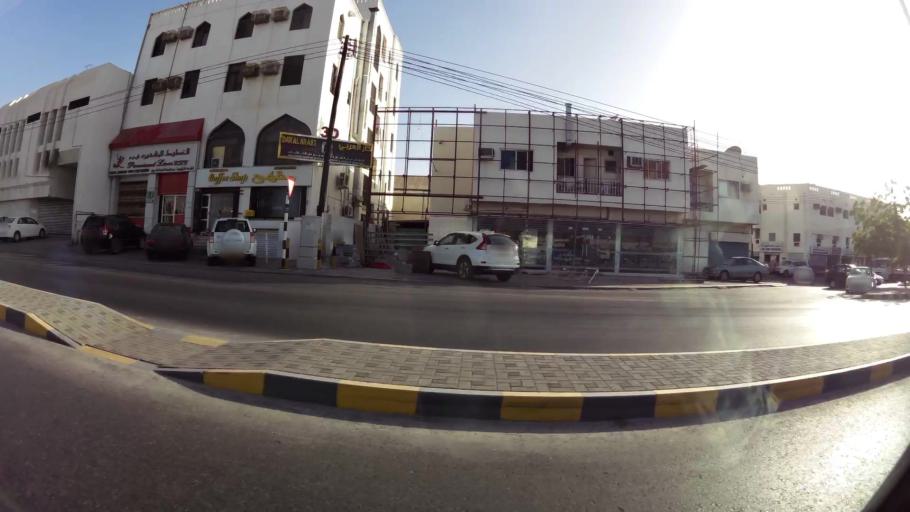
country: OM
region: Muhafazat Masqat
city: Muscat
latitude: 23.5878
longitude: 58.5526
